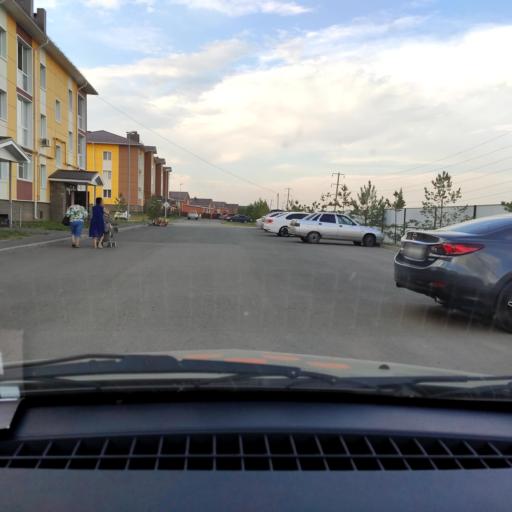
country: RU
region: Bashkortostan
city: Ufa
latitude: 54.5886
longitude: 55.9175
